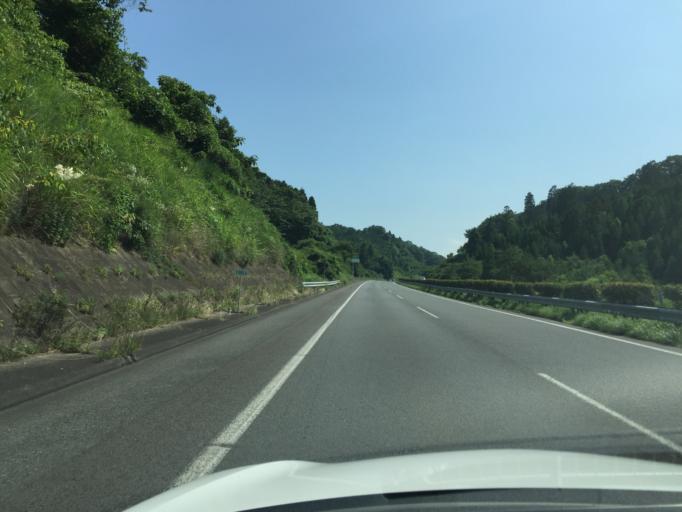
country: JP
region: Fukushima
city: Iwaki
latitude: 36.9948
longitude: 140.8061
